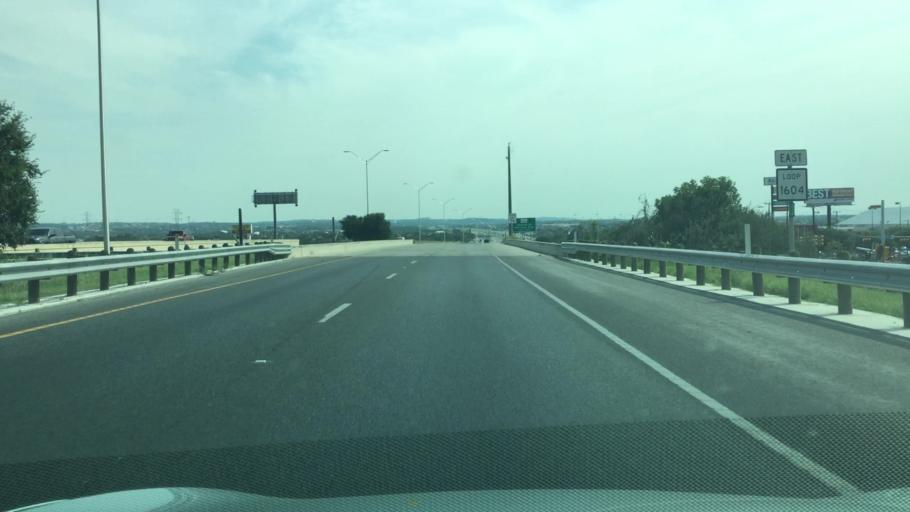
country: US
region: Texas
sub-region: Bexar County
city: Helotes
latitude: 29.5529
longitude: -98.6676
